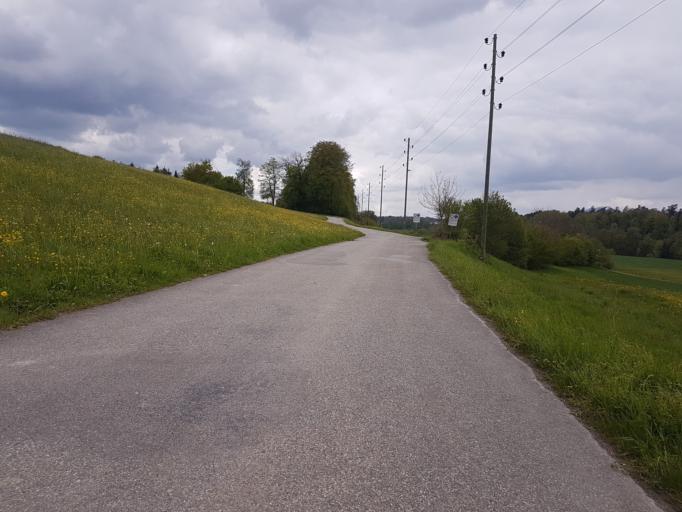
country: CH
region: Bern
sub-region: Oberaargau
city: Aarwangen
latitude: 47.2427
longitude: 7.7560
